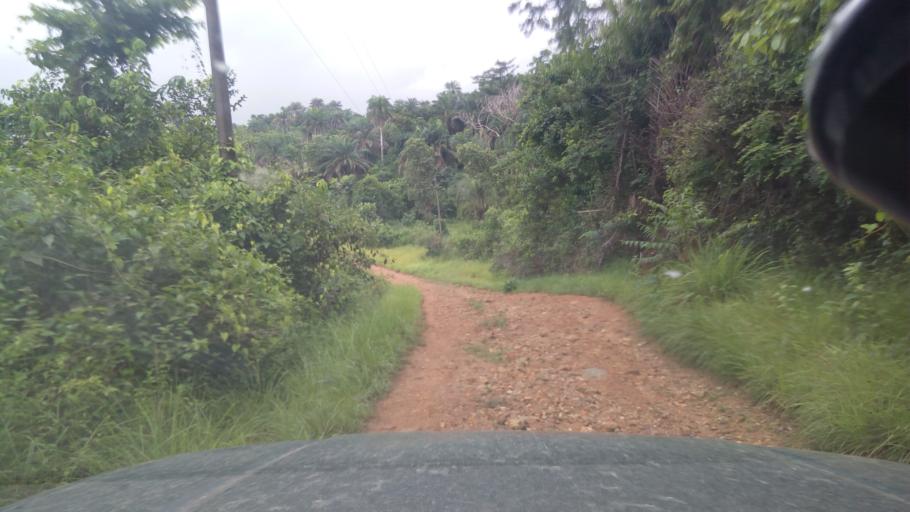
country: SL
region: Eastern Province
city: Boajibu
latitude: 8.1455
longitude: -11.2525
